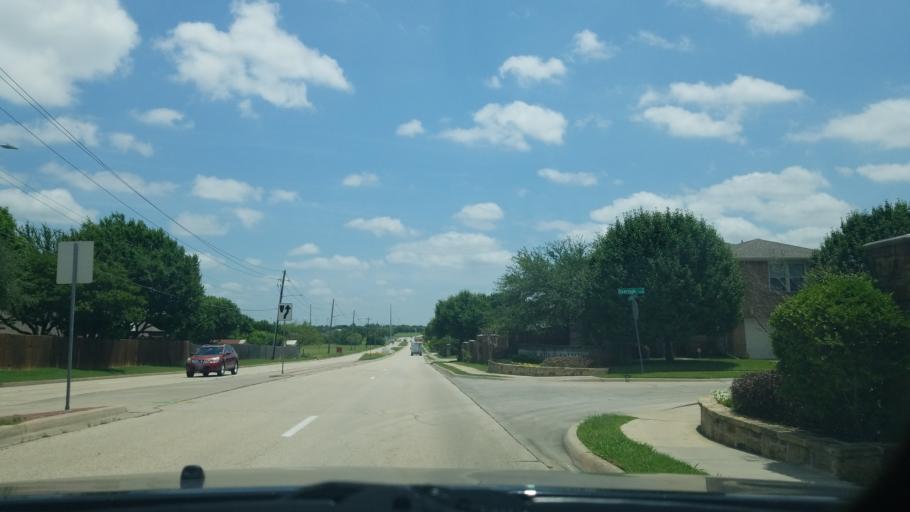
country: US
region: Texas
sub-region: Denton County
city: Denton
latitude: 33.2397
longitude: -97.1665
